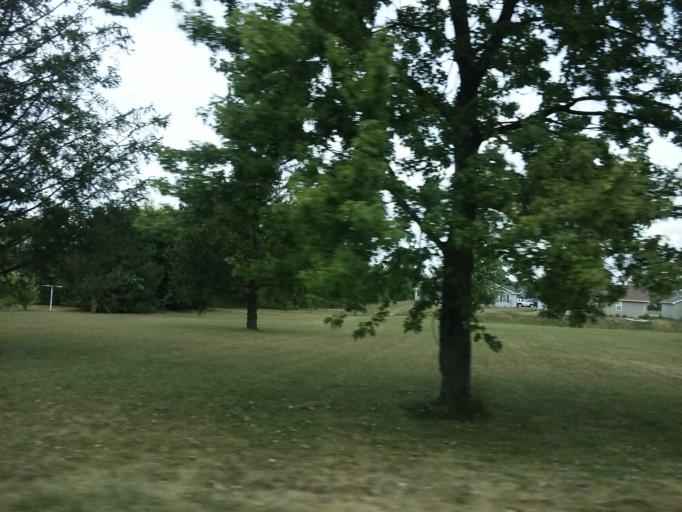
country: US
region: Ohio
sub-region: Hancock County
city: Findlay
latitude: 41.0419
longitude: -83.6835
